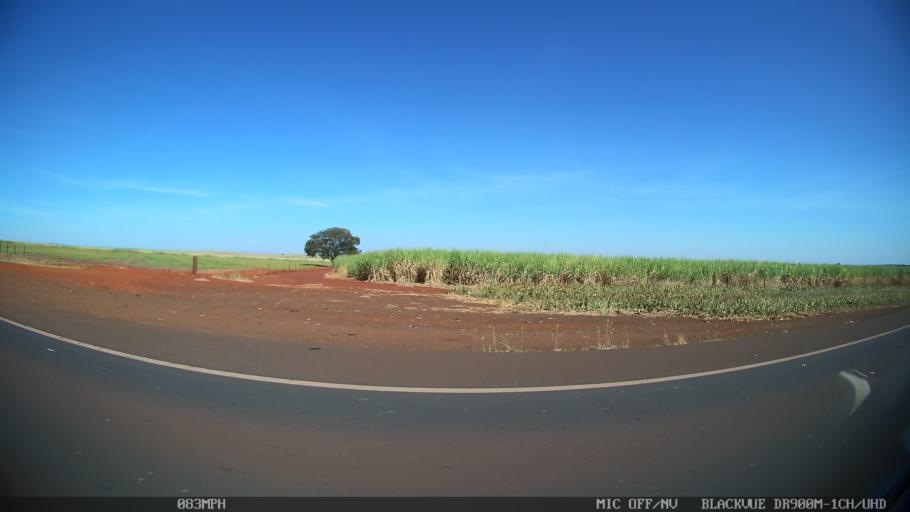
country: BR
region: Sao Paulo
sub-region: Ipua
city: Ipua
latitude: -20.4694
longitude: -48.1144
